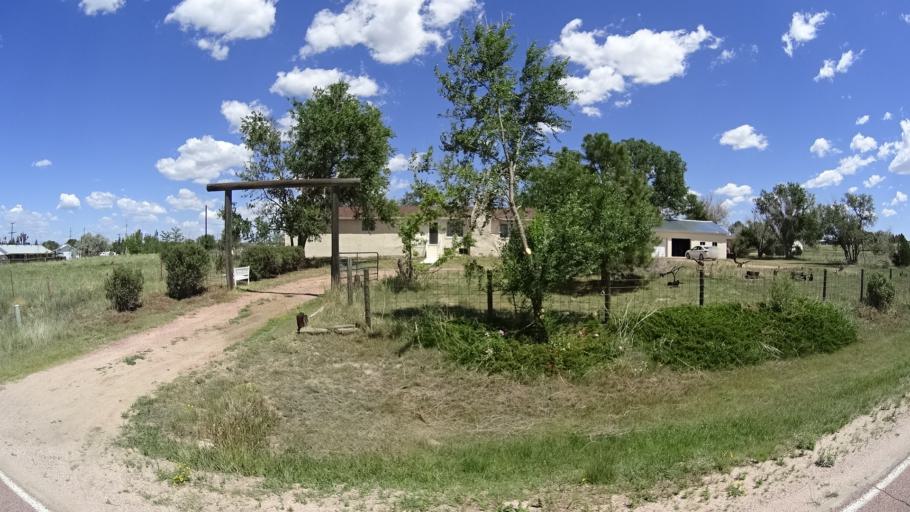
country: US
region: Colorado
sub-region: El Paso County
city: Cimarron Hills
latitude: 38.9116
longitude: -104.6229
